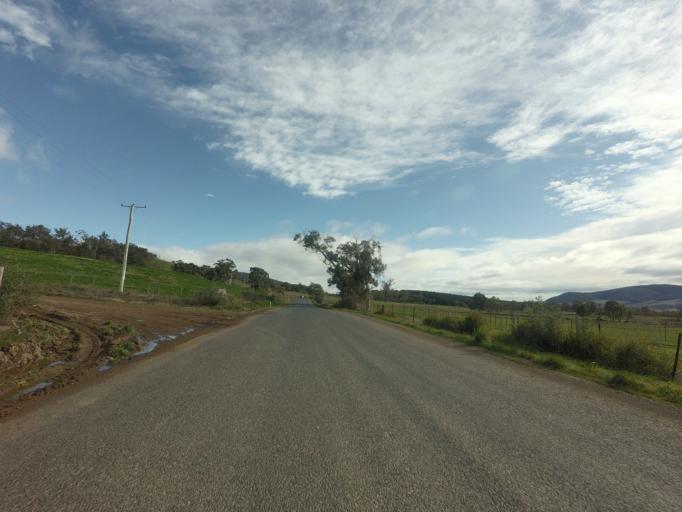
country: AU
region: Tasmania
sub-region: Derwent Valley
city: New Norfolk
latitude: -42.7776
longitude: 146.9818
